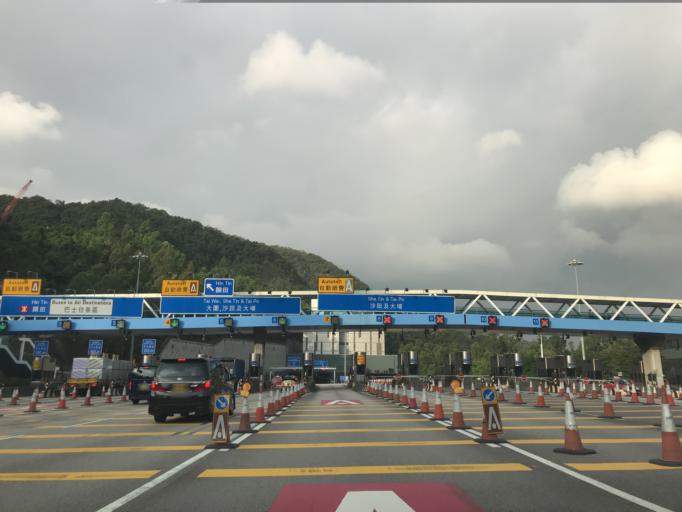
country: HK
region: Wong Tai Sin
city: Wong Tai Sin
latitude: 22.3588
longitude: 114.1628
